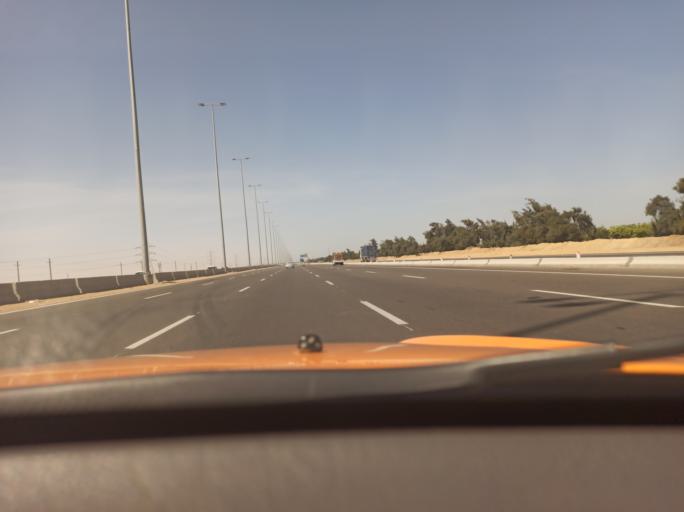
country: EG
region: Al Isma'iliyah
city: At Tall al Kabir
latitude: 30.4215
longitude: 32.0279
